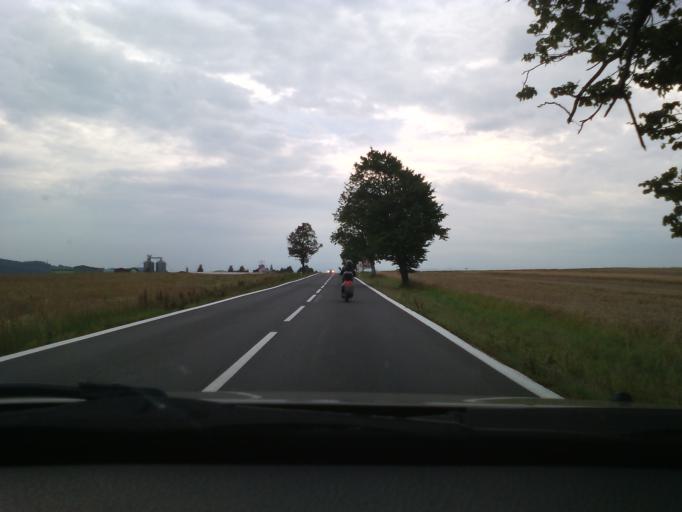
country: SK
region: Presovsky
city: Spisska Bela
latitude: 49.1996
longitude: 20.4687
